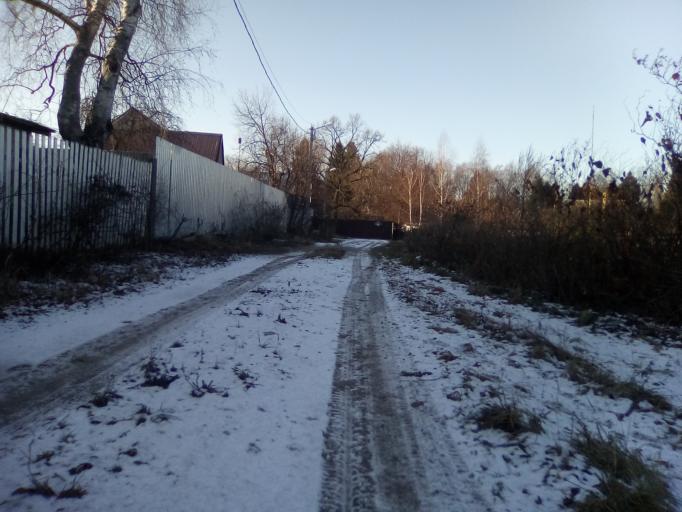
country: RU
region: Moskovskaya
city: Lesnoy Gorodok
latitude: 55.6491
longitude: 37.1703
